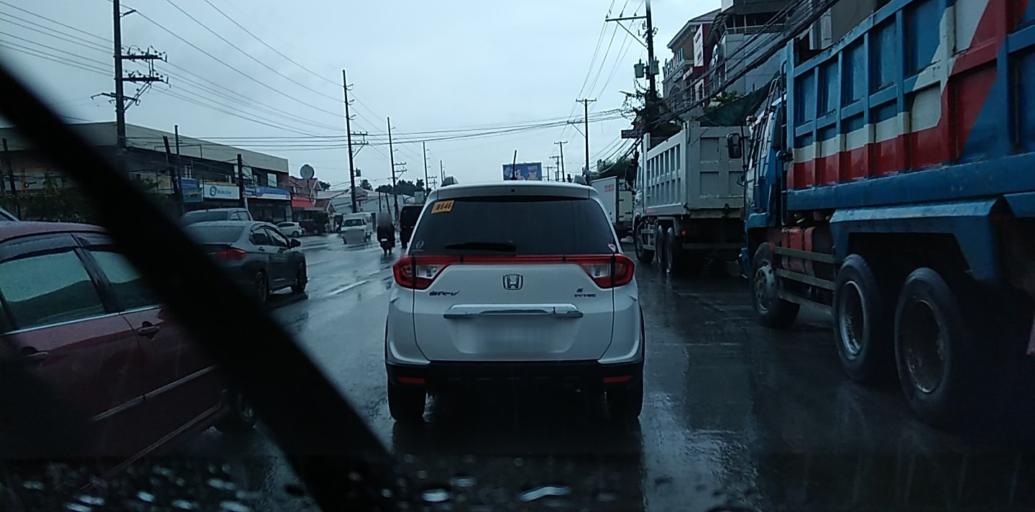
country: PH
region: Central Luzon
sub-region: Province of Pampanga
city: Magliman
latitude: 15.0507
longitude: 120.6646
